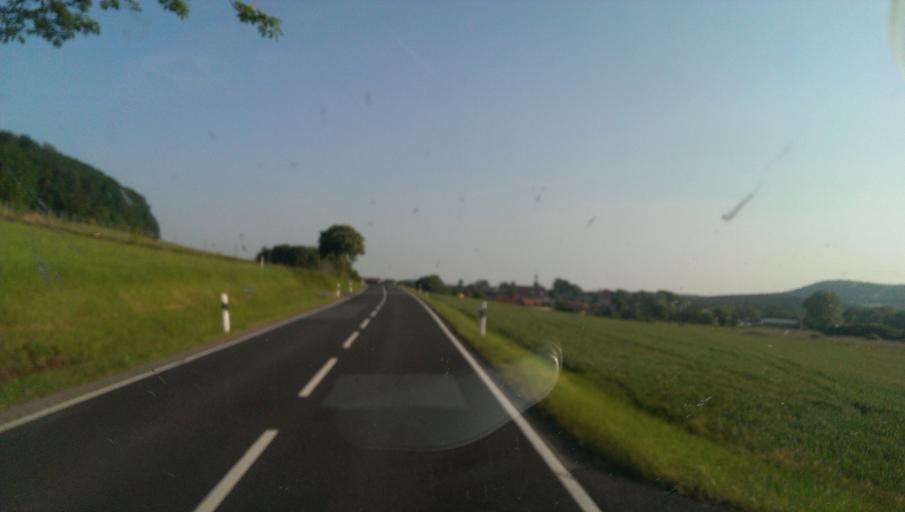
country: DE
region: Thuringia
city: Wolfershausen
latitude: 50.4621
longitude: 10.4390
